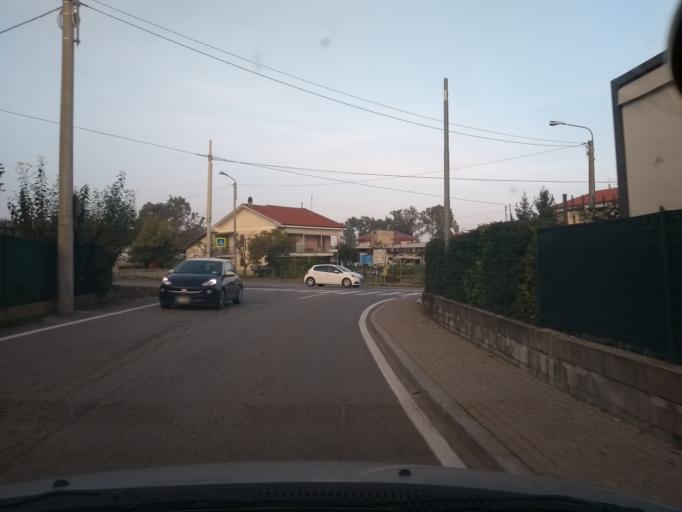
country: IT
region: Piedmont
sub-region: Provincia di Torino
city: La Cassa
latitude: 45.1828
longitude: 7.5159
